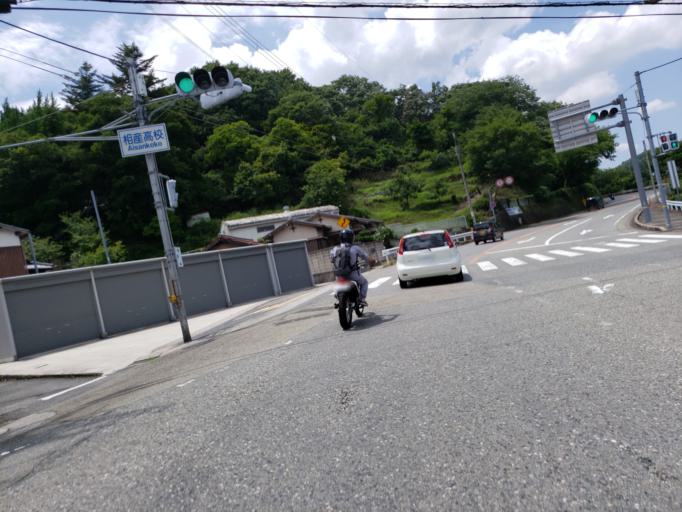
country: JP
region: Hyogo
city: Aioi
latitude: 34.8013
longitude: 134.4543
